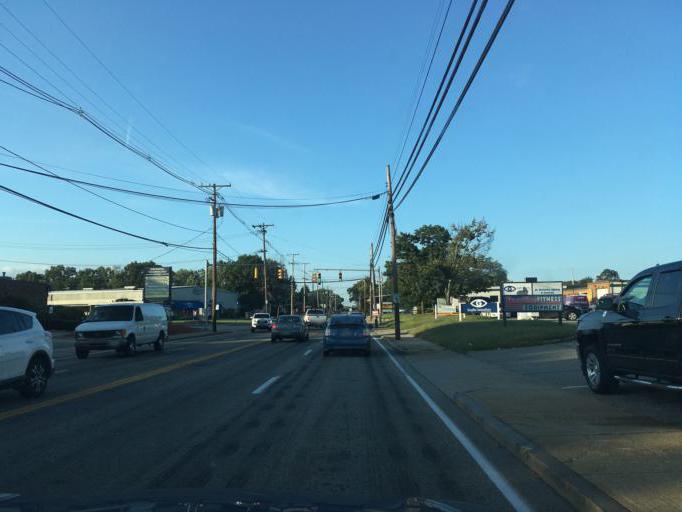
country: US
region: Rhode Island
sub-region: Providence County
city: Cranston
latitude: 41.7366
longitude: -71.4401
